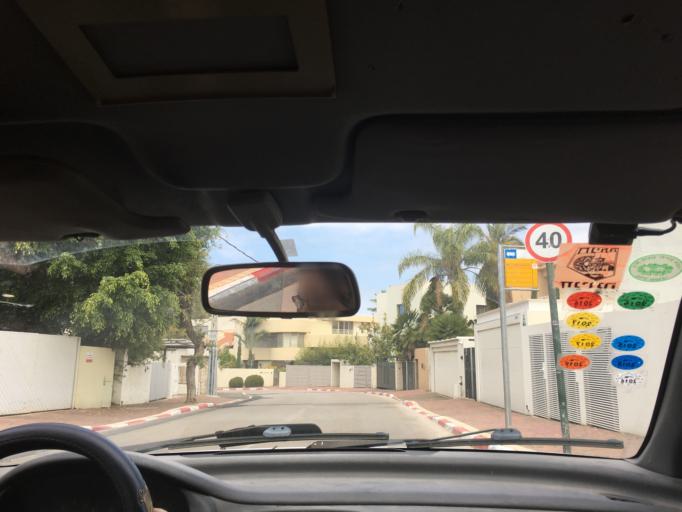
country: IL
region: Tel Aviv
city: Ramat HaSharon
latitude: 32.1416
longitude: 34.8299
